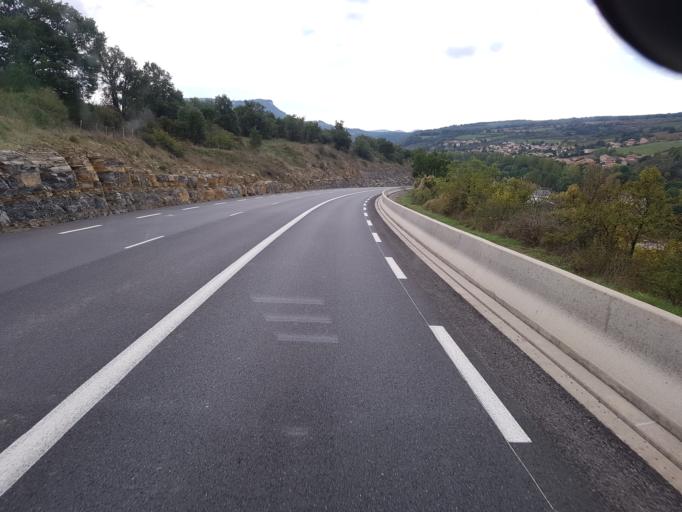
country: FR
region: Midi-Pyrenees
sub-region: Departement de l'Aveyron
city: Saint-Georges-de-Luzencon
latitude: 44.0740
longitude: 2.9893
